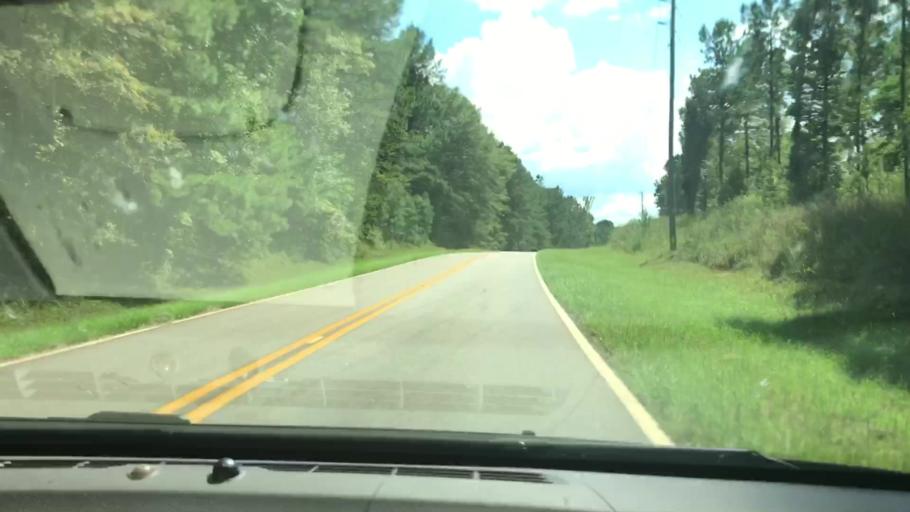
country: US
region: Georgia
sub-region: Troup County
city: La Grange
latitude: 33.1420
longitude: -85.1155
